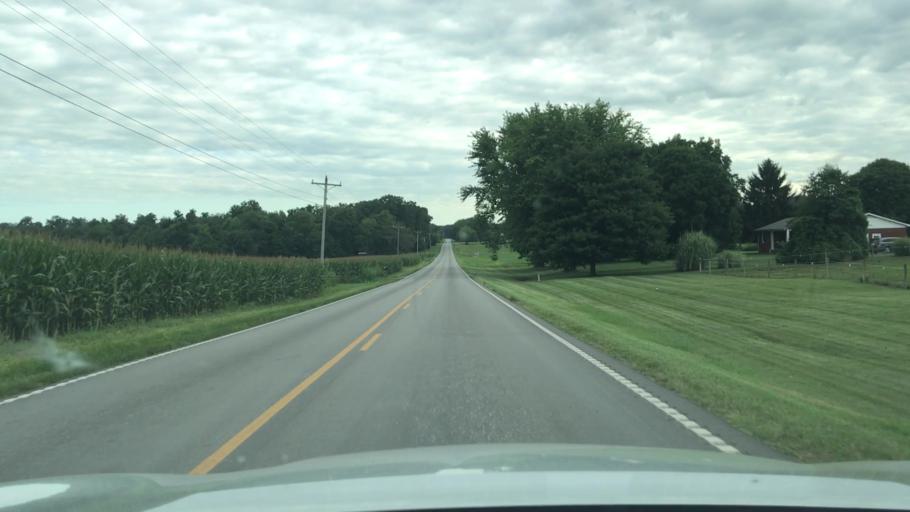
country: US
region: Kentucky
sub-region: Todd County
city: Guthrie
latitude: 36.7109
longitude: -87.1936
